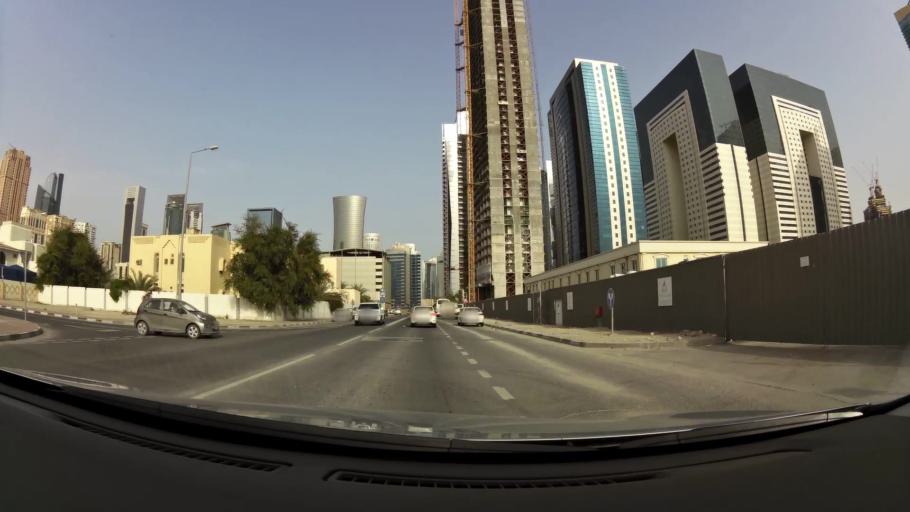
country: QA
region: Baladiyat ad Dawhah
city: Doha
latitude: 25.3202
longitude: 51.5191
